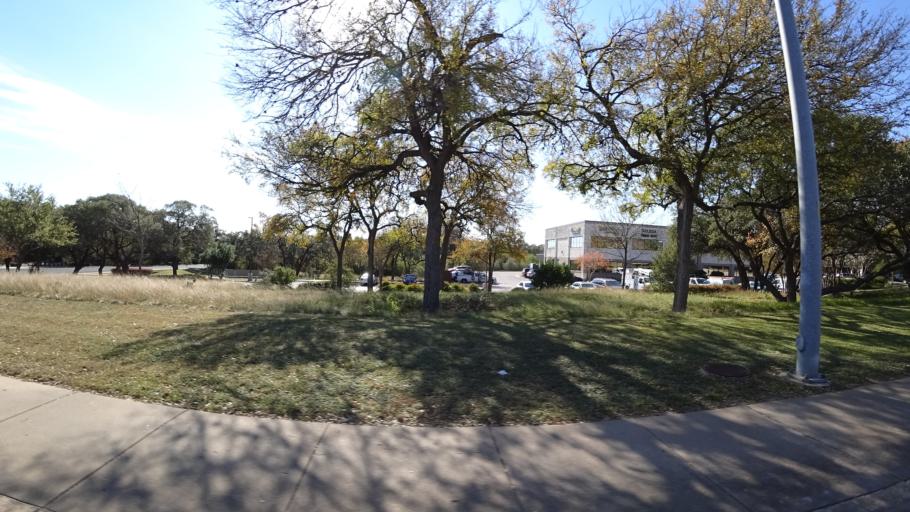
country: US
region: Texas
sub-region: Travis County
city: Barton Creek
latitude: 30.2284
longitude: -97.8622
